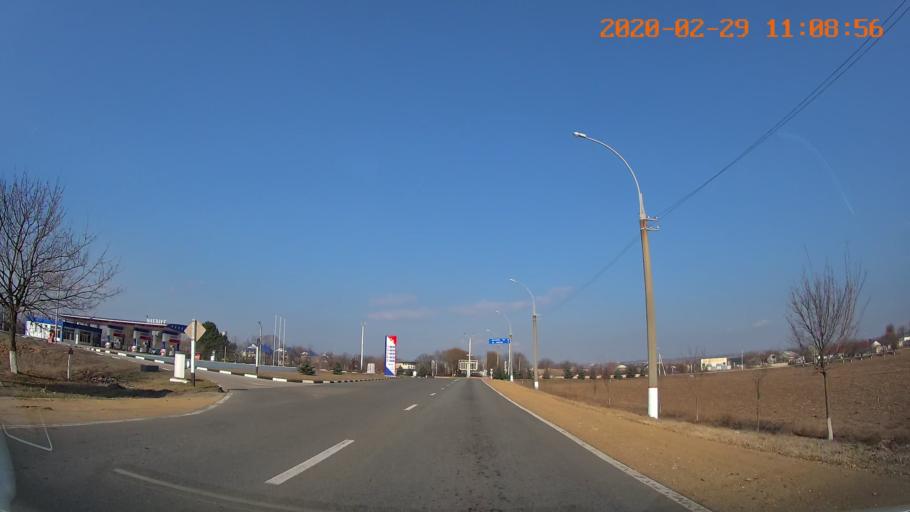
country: MD
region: Telenesti
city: Dubasari
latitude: 47.2382
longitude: 29.1722
